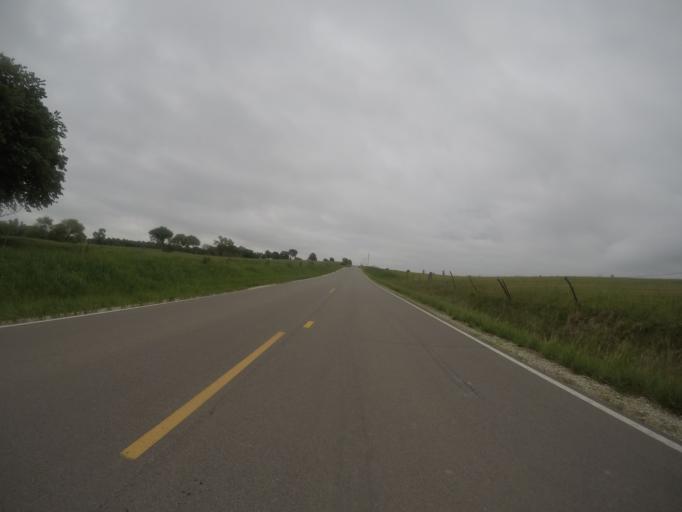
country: US
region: Kansas
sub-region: Pottawatomie County
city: Westmoreland
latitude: 39.5077
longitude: -96.1831
